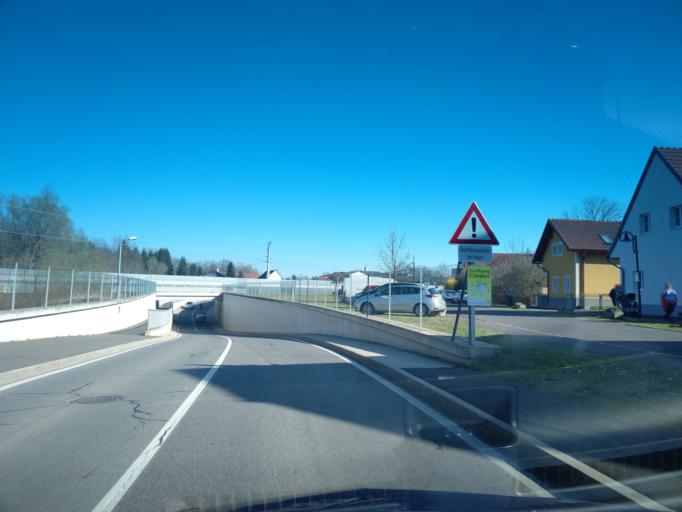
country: AT
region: Styria
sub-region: Politischer Bezirk Leibnitz
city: Stocking
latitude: 46.8610
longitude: 15.5297
